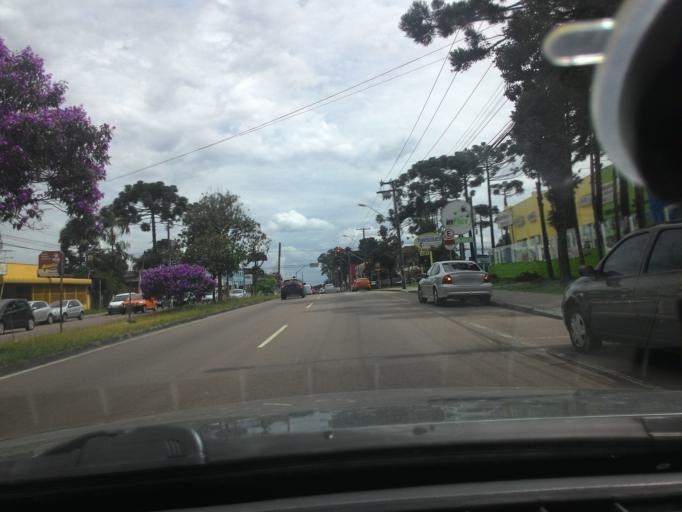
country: BR
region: Parana
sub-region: Pinhais
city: Pinhais
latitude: -25.4584
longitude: -49.2327
